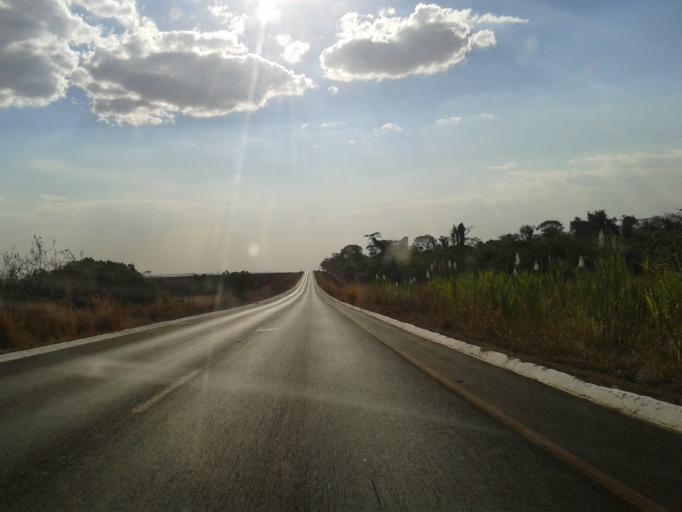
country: BR
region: Minas Gerais
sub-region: Centralina
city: Centralina
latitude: -18.7290
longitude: -49.2653
